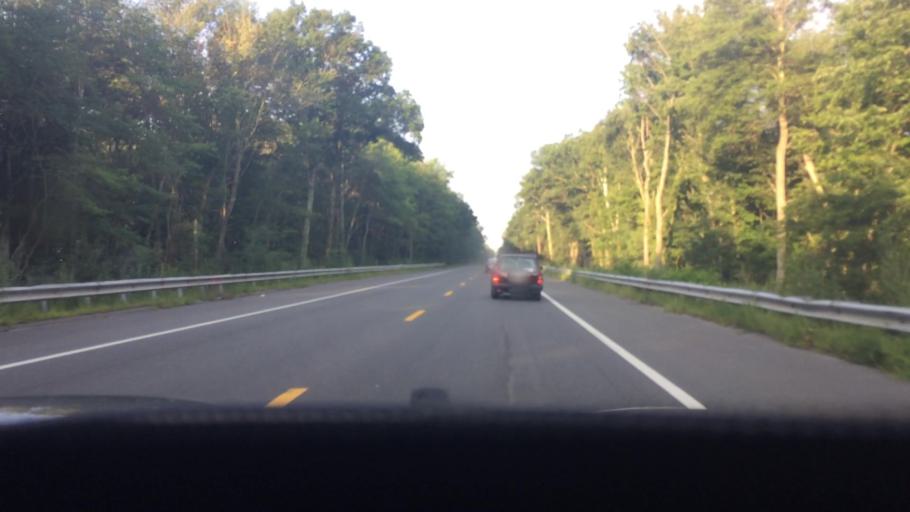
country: US
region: Massachusetts
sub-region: Middlesex County
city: North Reading
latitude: 42.6027
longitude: -71.1270
